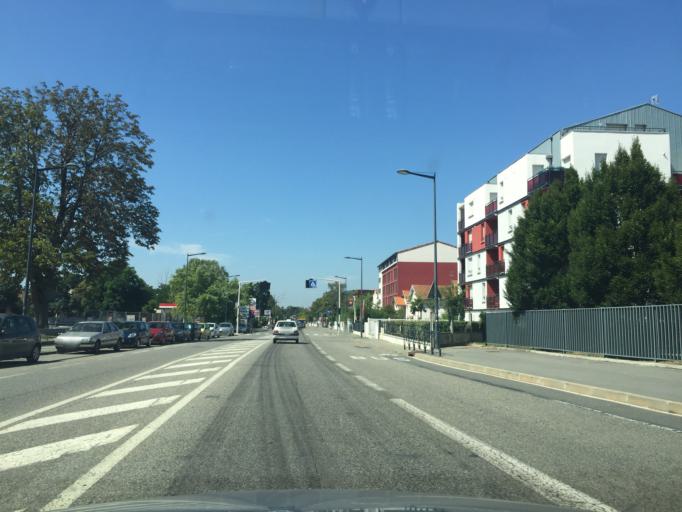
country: FR
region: Midi-Pyrenees
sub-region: Departement de la Haute-Garonne
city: Ramonville-Saint-Agne
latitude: 43.5653
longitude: 1.4598
